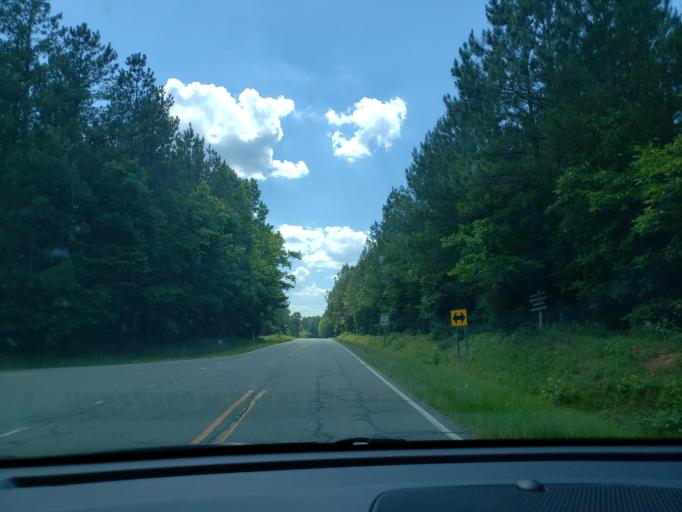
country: US
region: North Carolina
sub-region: Orange County
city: Chapel Hill
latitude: 36.0009
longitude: -79.0431
